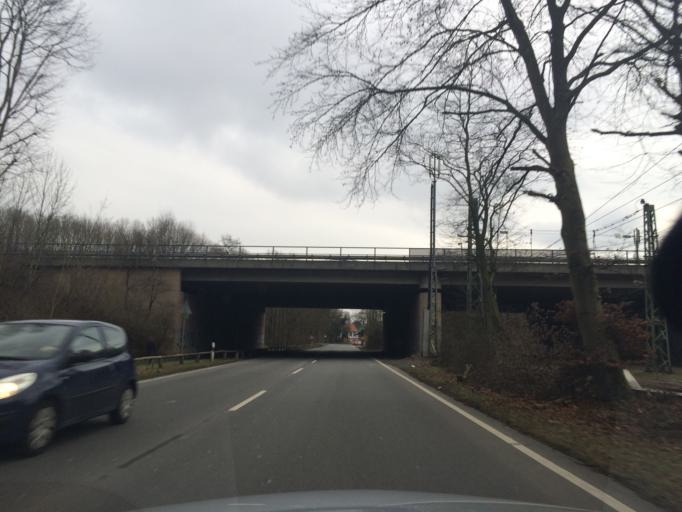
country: DE
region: Hesse
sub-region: Regierungsbezirk Darmstadt
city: Neu Isenburg
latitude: 50.0621
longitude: 8.6948
